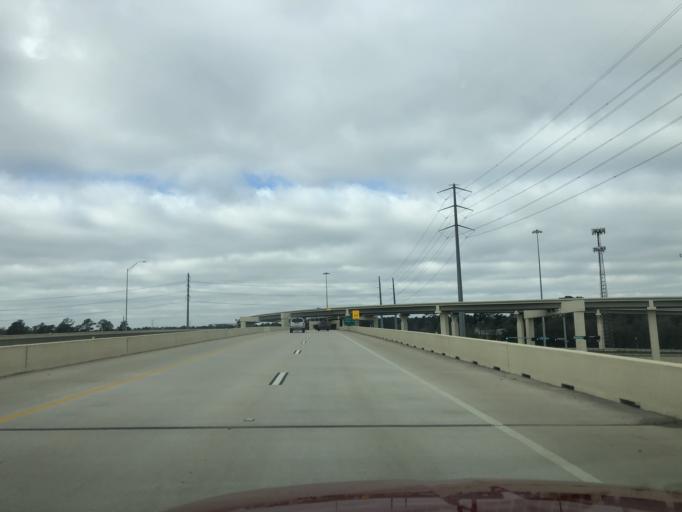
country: US
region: Texas
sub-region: Harris County
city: Spring
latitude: 30.0928
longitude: -95.4335
